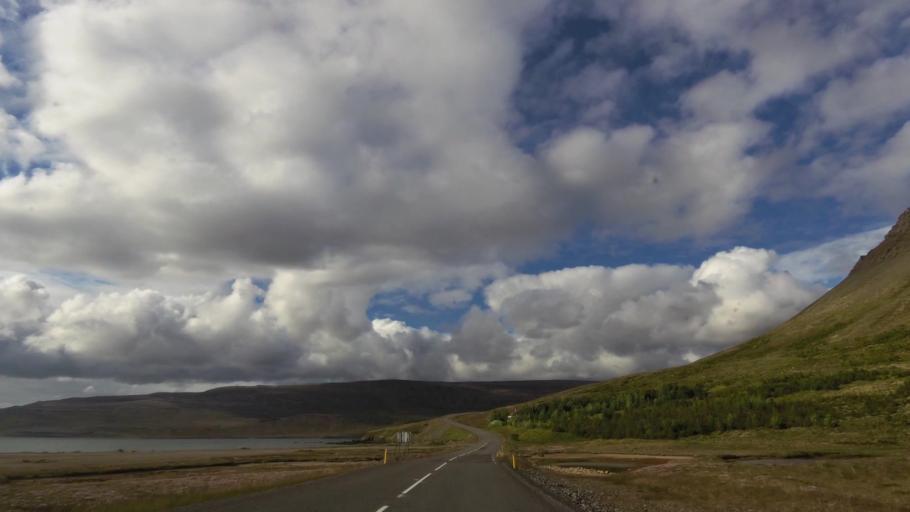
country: IS
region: West
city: Olafsvik
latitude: 65.5165
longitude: -23.8345
